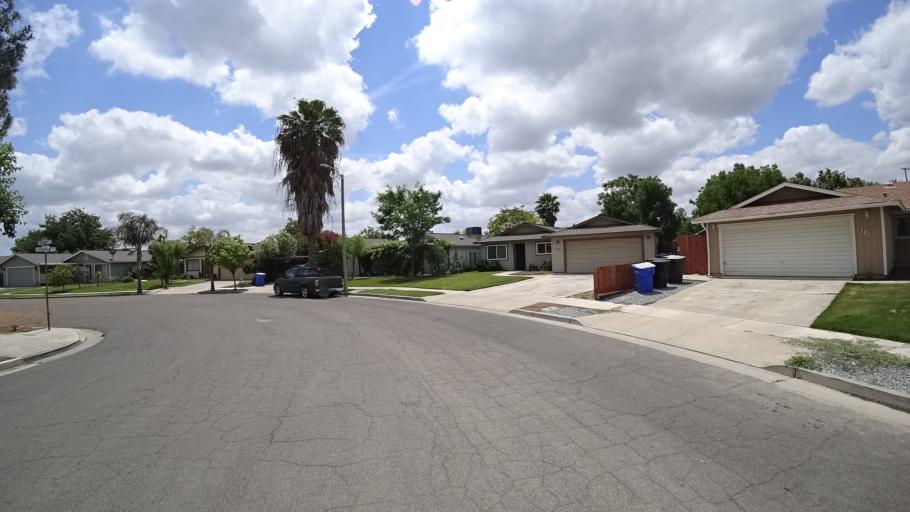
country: US
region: California
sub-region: Kings County
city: Hanford
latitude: 36.3103
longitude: -119.6721
